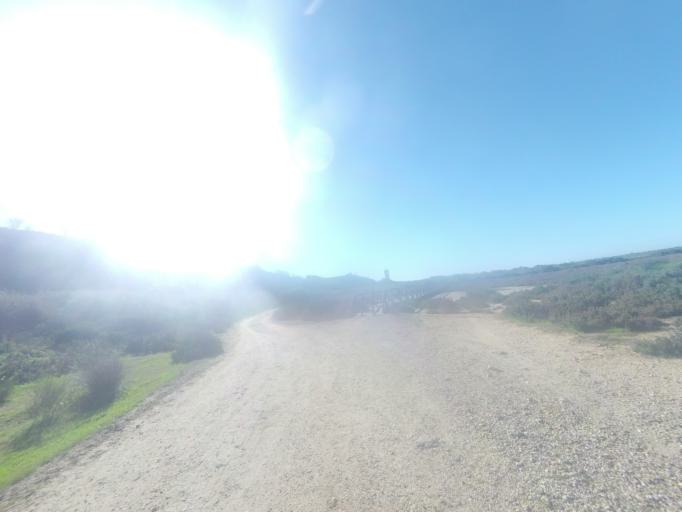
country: ES
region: Andalusia
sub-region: Provincia de Huelva
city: Palos de la Frontera
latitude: 37.2414
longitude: -6.8892
